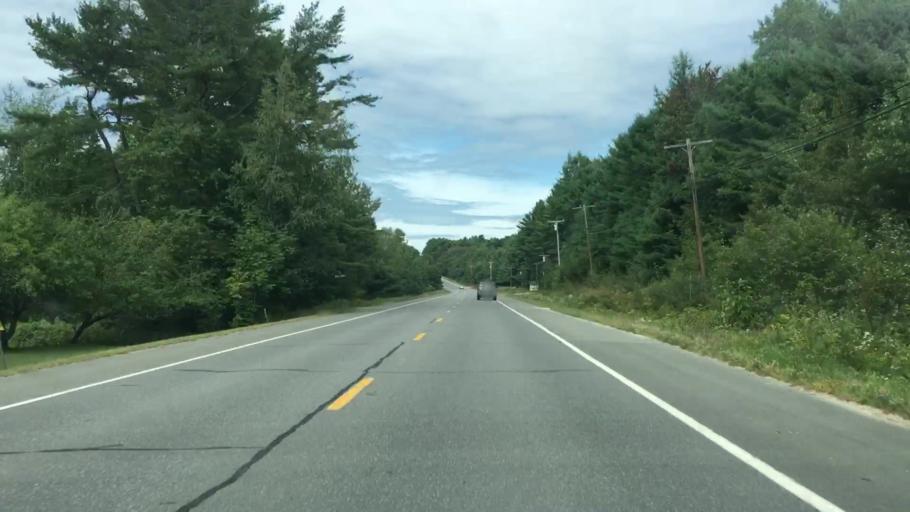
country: US
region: Maine
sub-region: Piscataquis County
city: Milo
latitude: 45.2744
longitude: -69.0020
